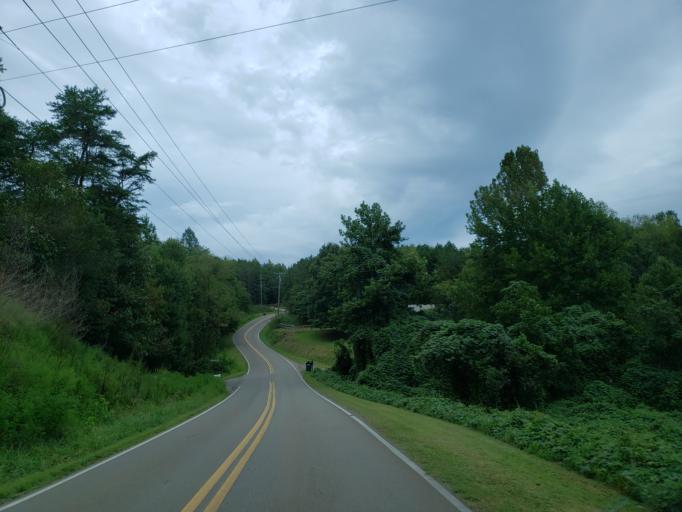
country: US
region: Georgia
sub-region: Pickens County
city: Jasper
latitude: 34.4200
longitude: -84.5540
